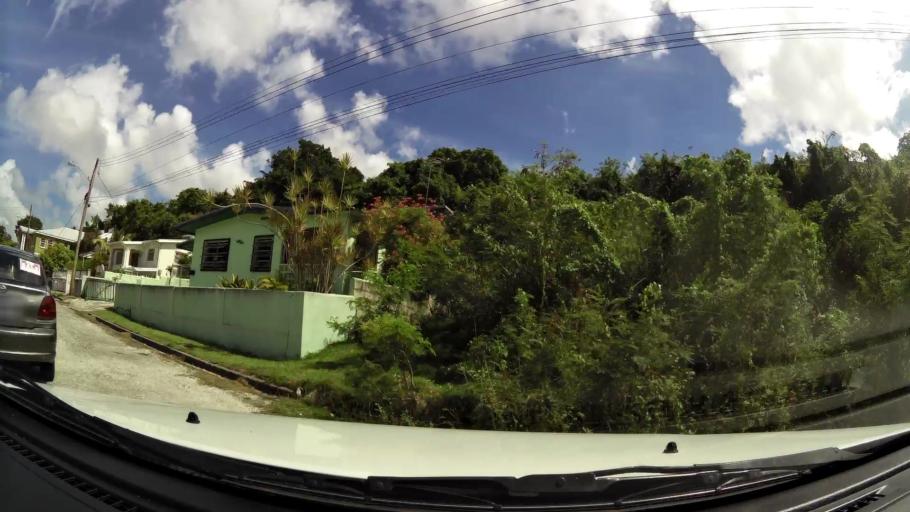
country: BB
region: Saint James
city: Holetown
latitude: 13.1533
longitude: -59.6340
